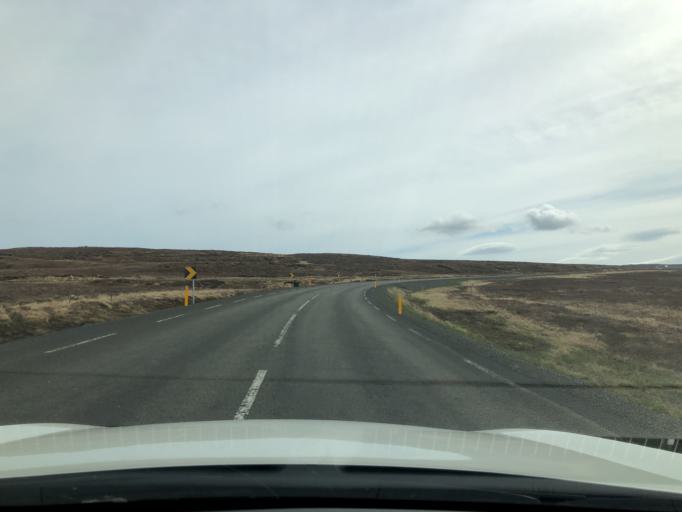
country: IS
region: East
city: Egilsstadir
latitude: 65.4308
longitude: -14.5915
